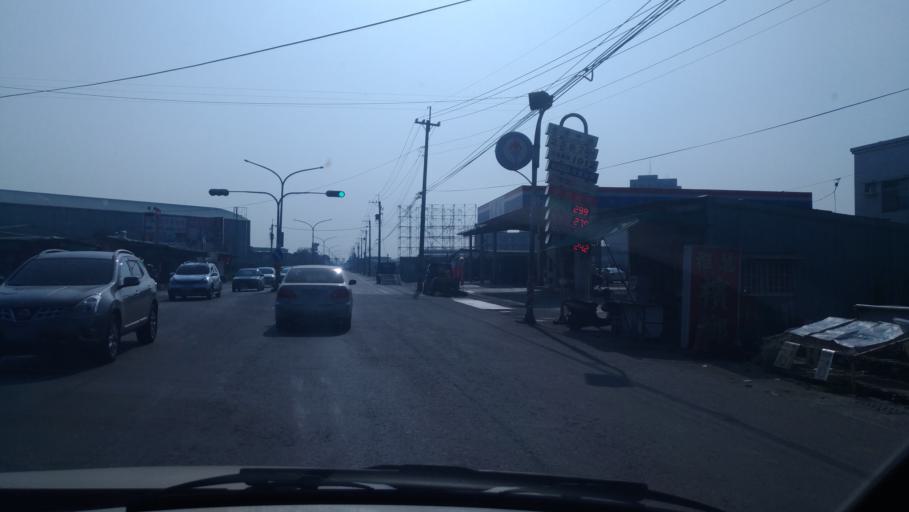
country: TW
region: Taiwan
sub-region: Chiayi
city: Jiayi Shi
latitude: 23.5228
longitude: 120.4233
